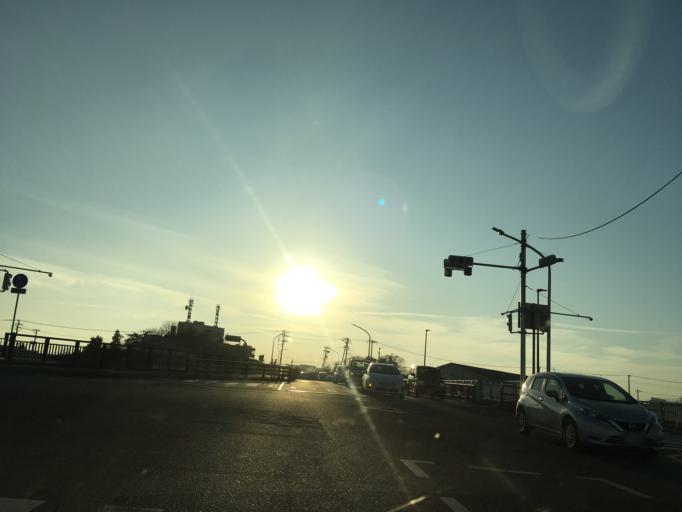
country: JP
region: Miyagi
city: Wakuya
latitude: 38.6858
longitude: 141.2006
